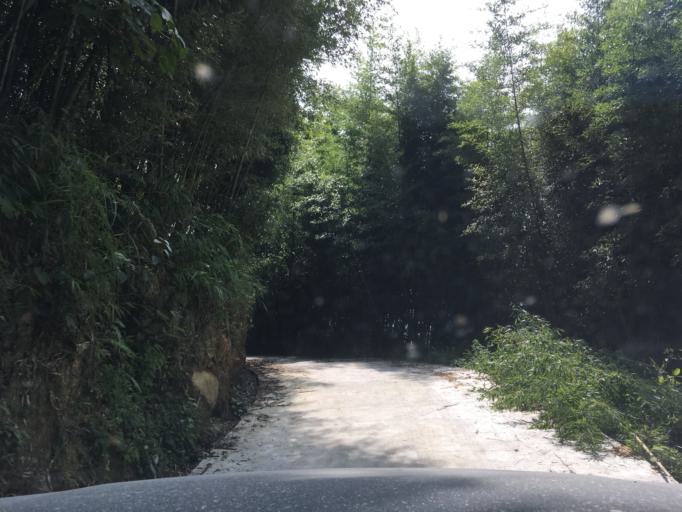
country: CN
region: Guangxi Zhuangzu Zizhiqu
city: Xinzhou
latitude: 24.9710
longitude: 105.6219
